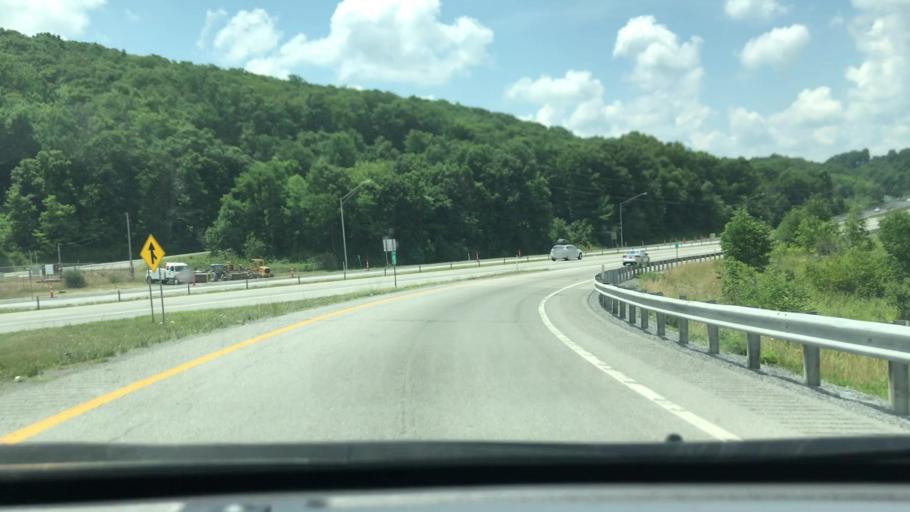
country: US
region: West Virginia
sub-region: Mercer County
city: Princeton
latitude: 37.3619
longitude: -81.0504
